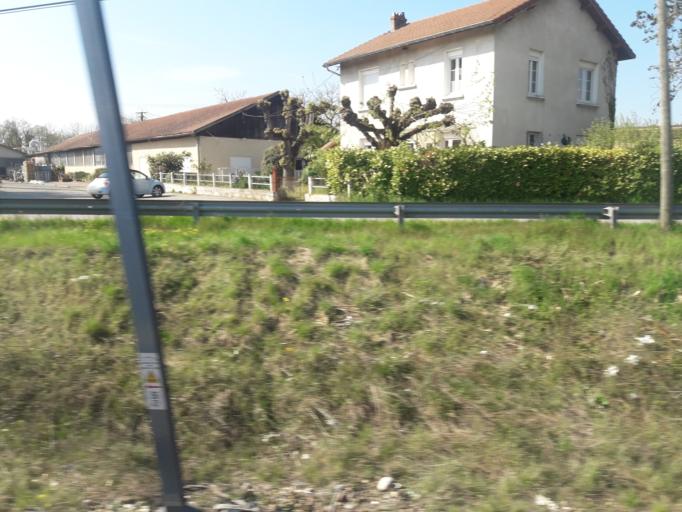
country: FR
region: Rhone-Alpes
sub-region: Departement de l'Isere
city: Saint-Hilaire-du-Rosier
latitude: 45.0731
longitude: 5.2498
